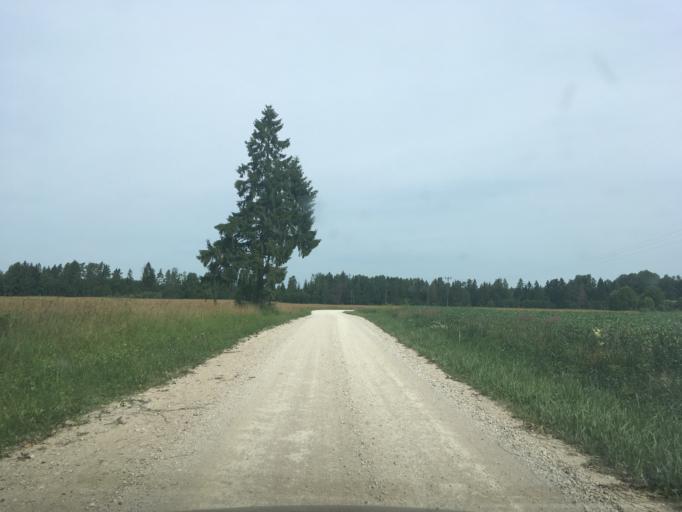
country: EE
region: Raplamaa
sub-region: Maerjamaa vald
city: Marjamaa
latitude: 58.9436
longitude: 24.5531
